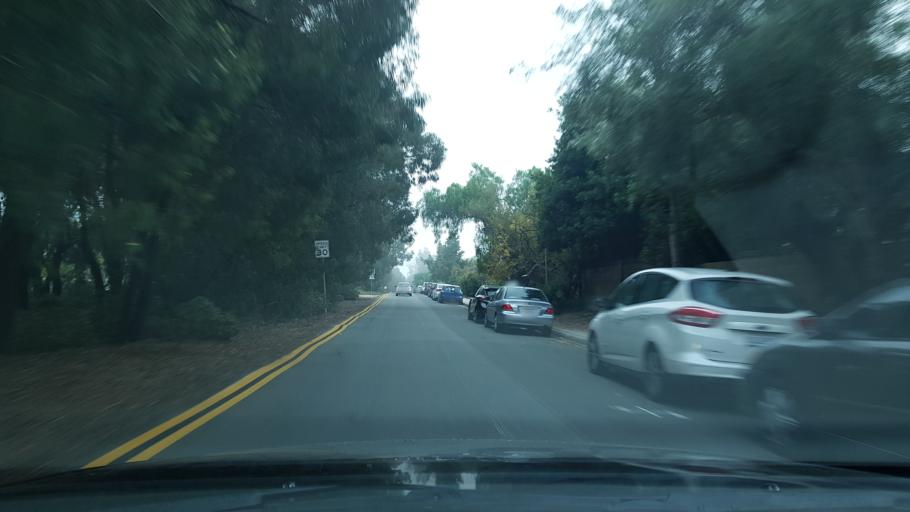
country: US
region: California
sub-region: San Diego County
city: La Jolla
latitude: 32.8615
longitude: -117.2402
